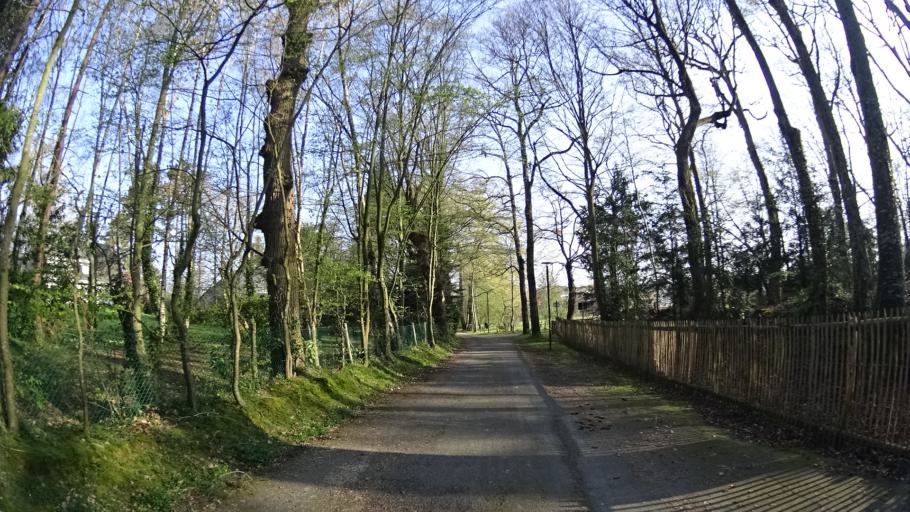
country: FR
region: Brittany
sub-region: Departement d'Ille-et-Vilaine
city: Pace
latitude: 48.1464
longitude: -1.7763
